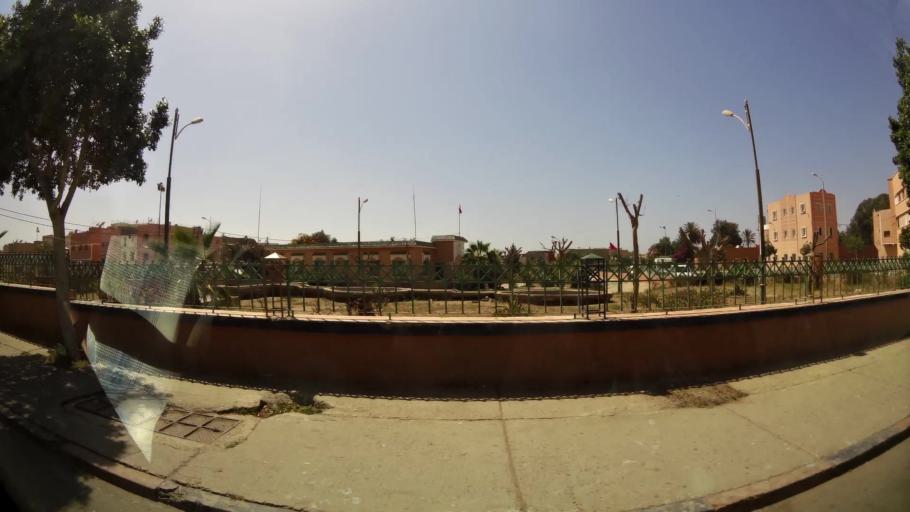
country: MA
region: Souss-Massa-Draa
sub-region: Inezgane-Ait Mellou
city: Inezgane
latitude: 30.3503
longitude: -9.5353
